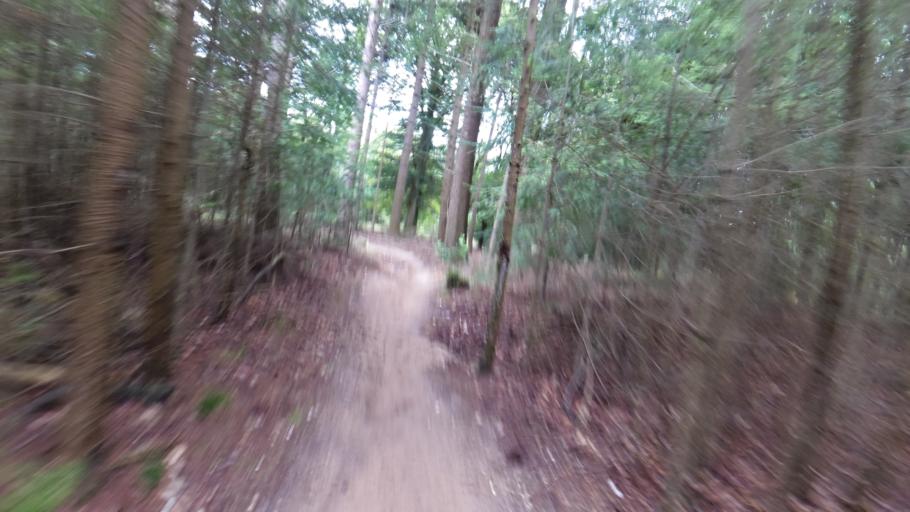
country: NL
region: Utrecht
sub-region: Gemeente Utrechtse Heuvelrug
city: Amerongen
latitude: 52.0044
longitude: 5.4732
